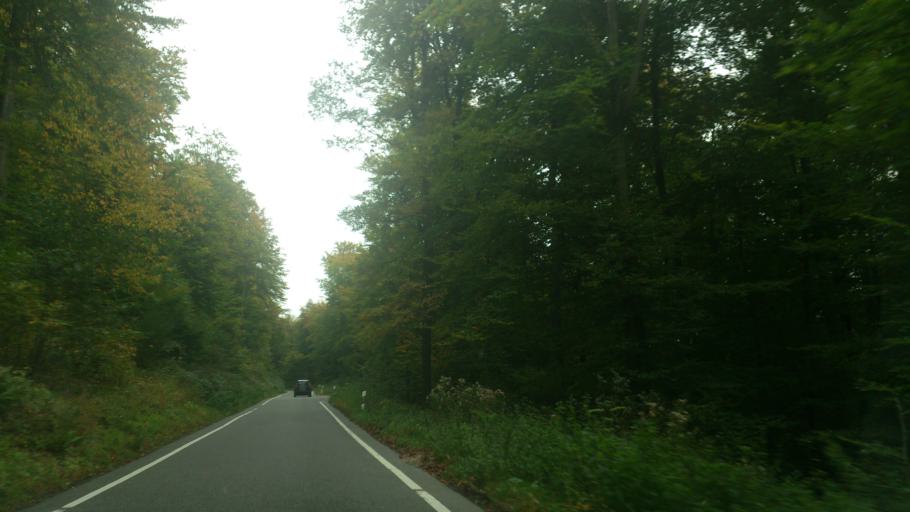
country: DE
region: Baden-Wuerttemberg
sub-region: Karlsruhe Region
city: Heidelberg
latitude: 49.3854
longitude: 8.7155
